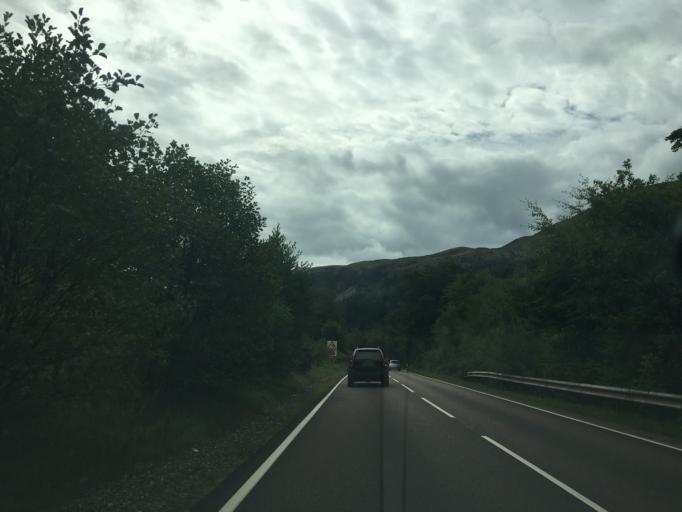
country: GB
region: Scotland
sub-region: Stirling
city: Callander
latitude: 56.2660
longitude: -4.2855
